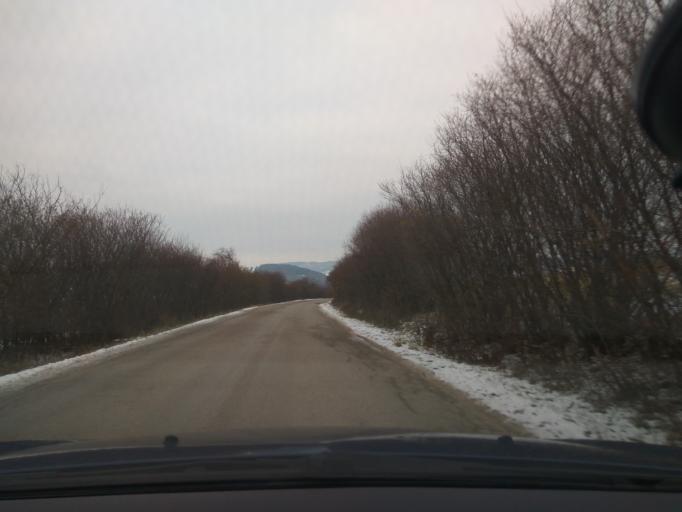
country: SK
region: Nitriansky
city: Stara Tura
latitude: 48.7978
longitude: 17.7178
